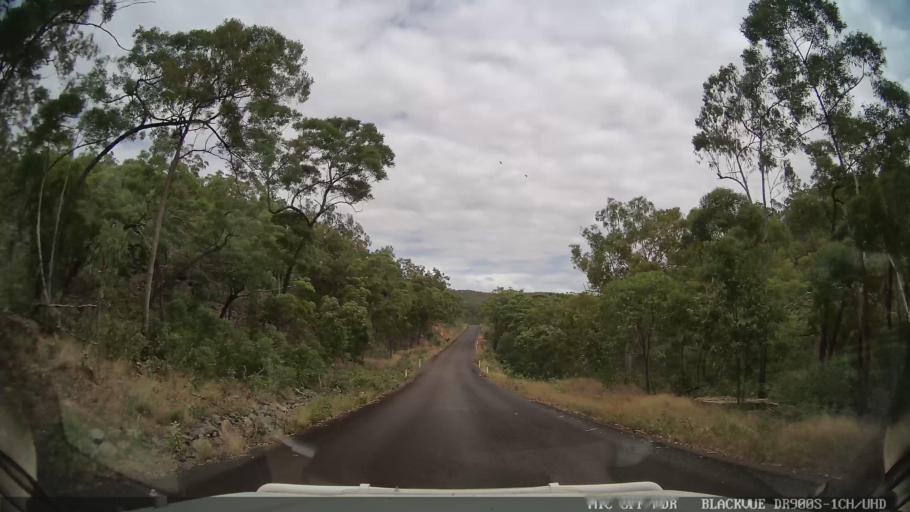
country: AU
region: Queensland
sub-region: Cook
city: Cooktown
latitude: -15.2835
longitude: 144.9064
